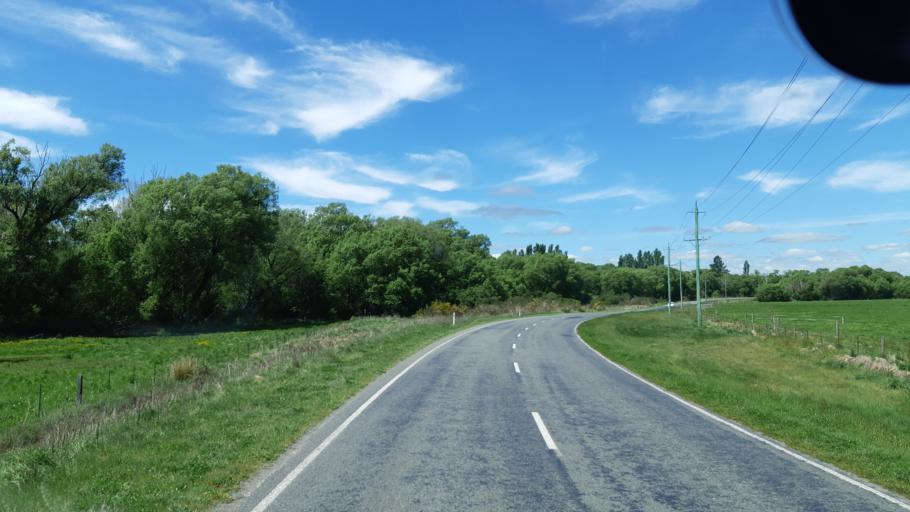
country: NZ
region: Canterbury
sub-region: Ashburton District
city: Methven
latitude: -43.7331
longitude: 171.5285
